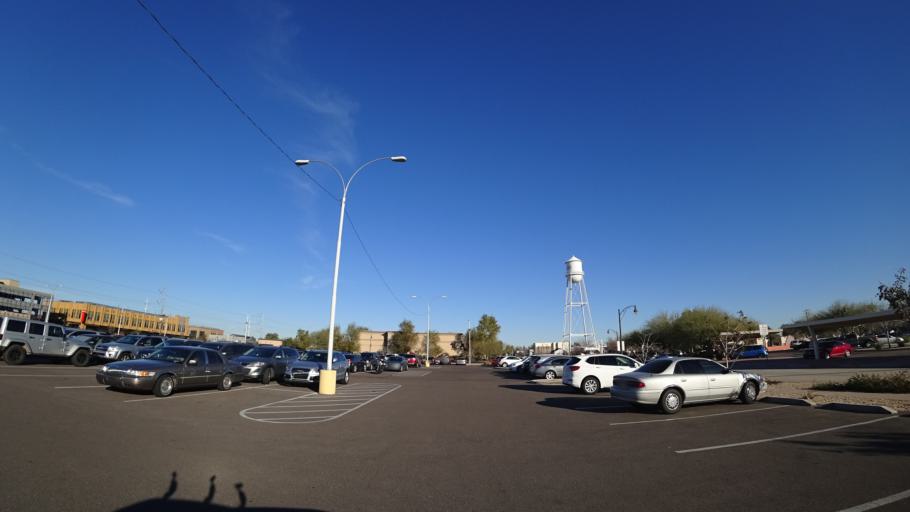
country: US
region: Arizona
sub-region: Maricopa County
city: Gilbert
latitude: 33.3550
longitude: -111.7919
